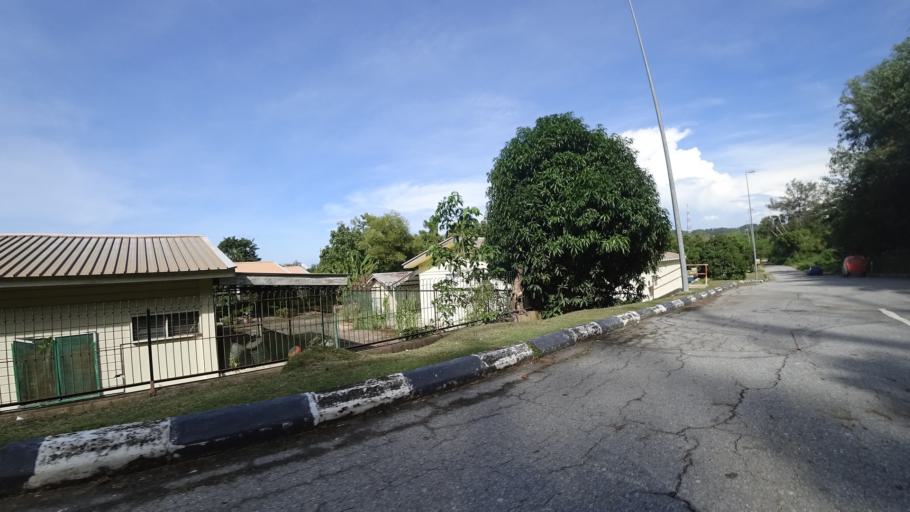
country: BN
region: Brunei and Muara
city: Bandar Seri Begawan
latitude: 4.9484
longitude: 114.8363
